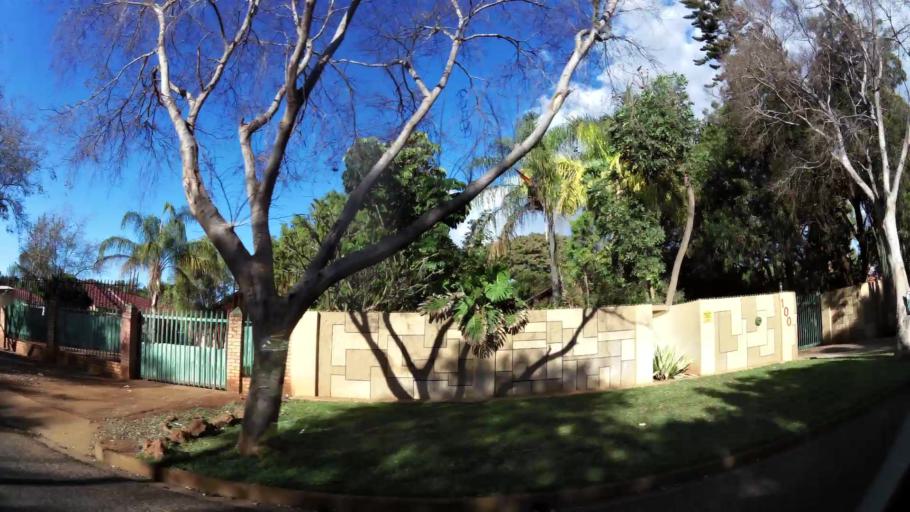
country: ZA
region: Limpopo
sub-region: Waterberg District Municipality
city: Mokopane
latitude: -24.1839
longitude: 28.9994
